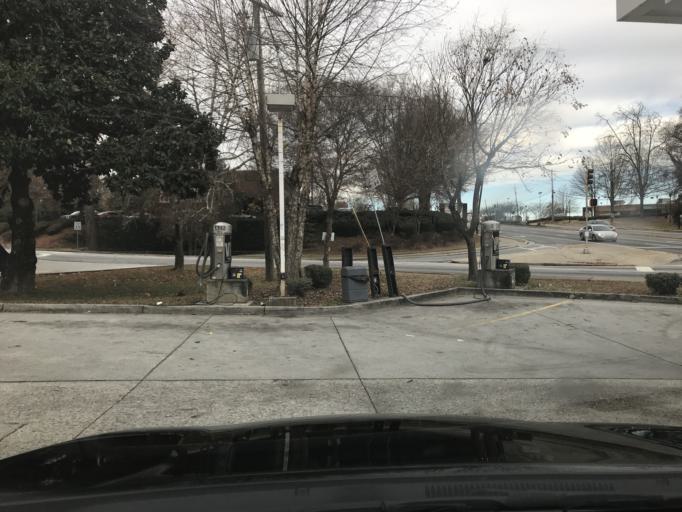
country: US
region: Georgia
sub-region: Fulton County
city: East Point
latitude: 33.7228
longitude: -84.5061
